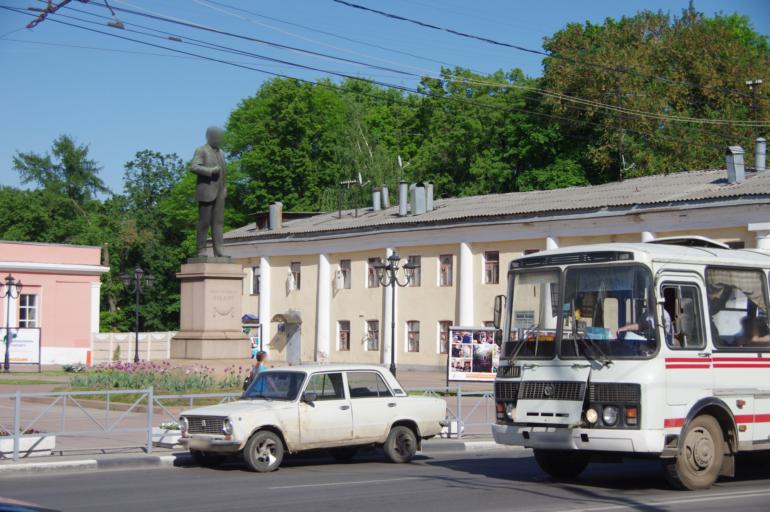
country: RU
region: Rjazan
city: Ryazan'
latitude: 54.6259
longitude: 39.7492
